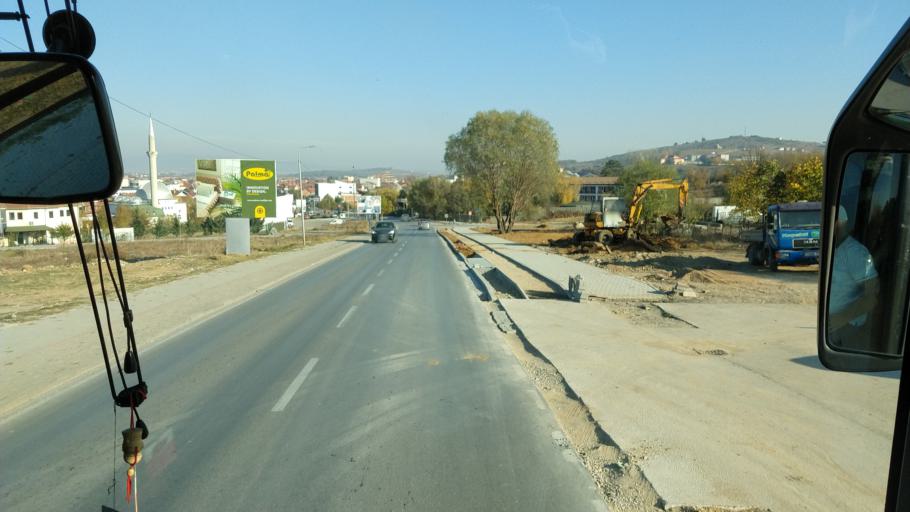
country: XK
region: Ferizaj
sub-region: Komuna e Shtimes
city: Shtime
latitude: 42.4357
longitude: 21.0265
